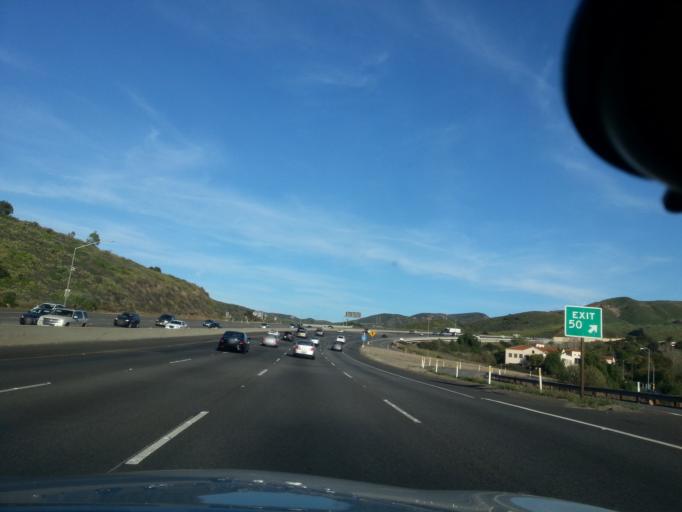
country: US
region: California
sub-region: Ventura County
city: Casa Conejo
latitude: 34.2053
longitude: -118.9866
